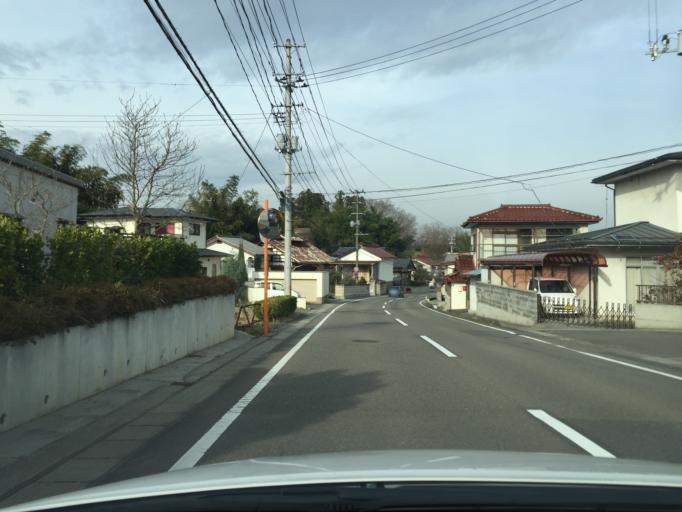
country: JP
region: Fukushima
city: Fukushima-shi
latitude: 37.6994
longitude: 140.4614
